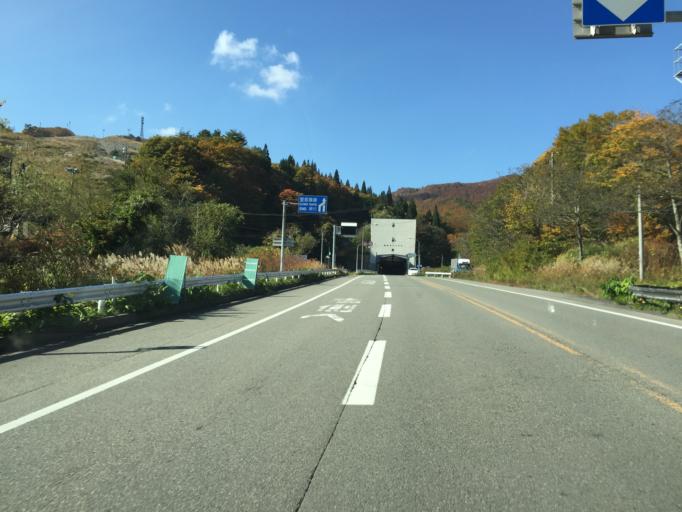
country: JP
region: Yamagata
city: Yonezawa
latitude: 37.8277
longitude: 140.2670
